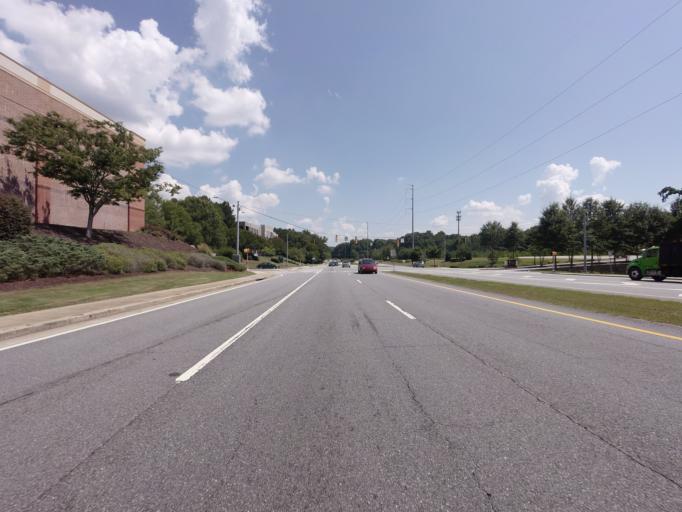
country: US
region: Georgia
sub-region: Fulton County
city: Johns Creek
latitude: 34.0128
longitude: -84.1842
